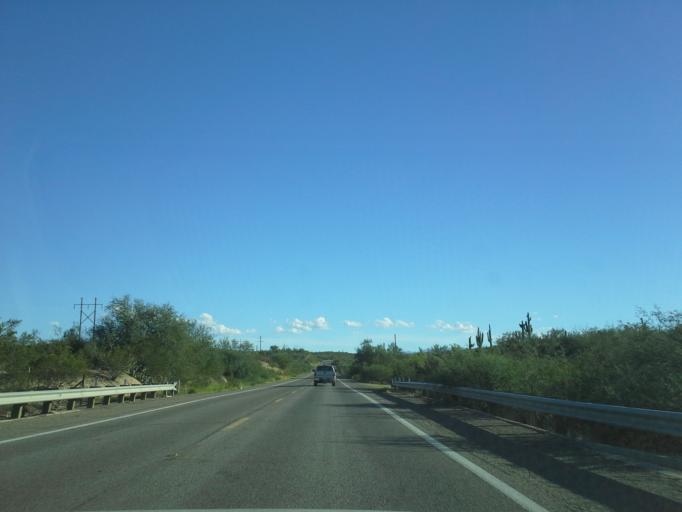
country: US
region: Arizona
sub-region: Pinal County
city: Mammoth
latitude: 32.8655
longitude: -110.7099
